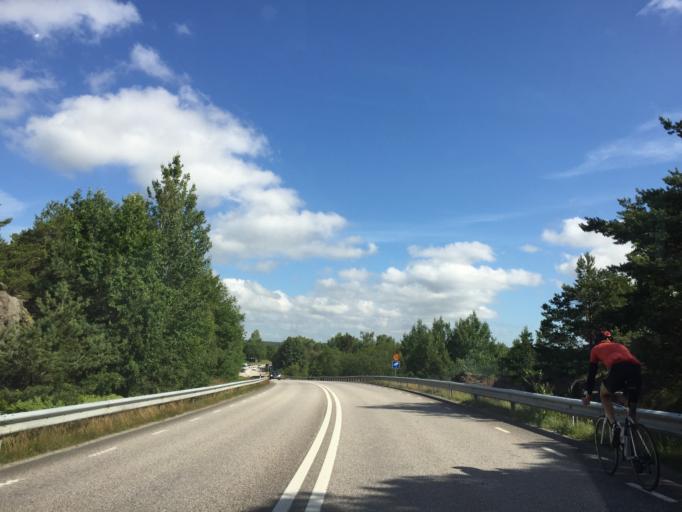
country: SE
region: Vaestra Goetaland
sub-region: Tjorns Kommun
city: Myggenas
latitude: 58.0887
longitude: 11.6997
